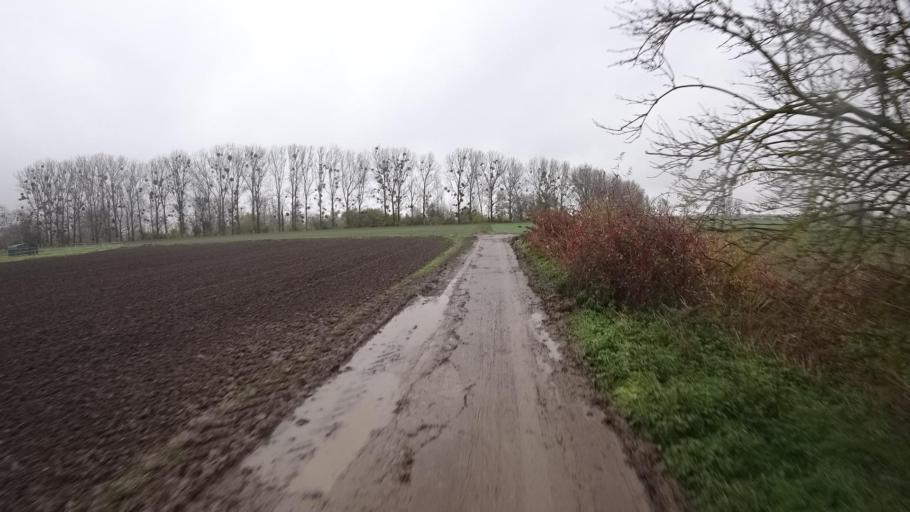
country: DE
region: Rheinland-Pfalz
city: Gimbsheim
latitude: 49.7975
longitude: 8.3717
